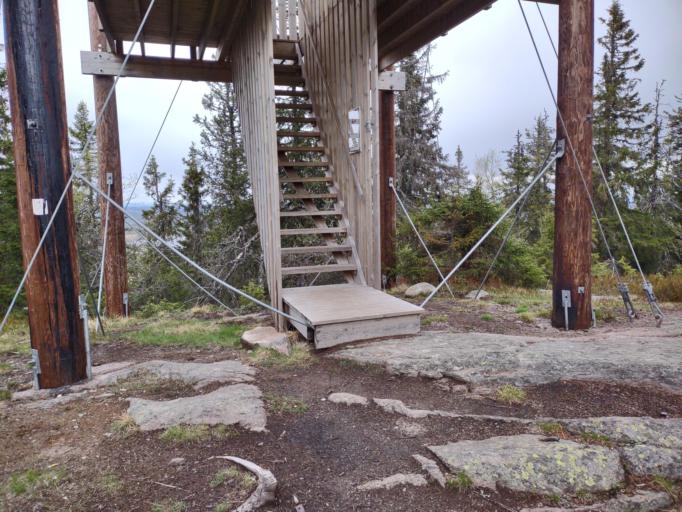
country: NO
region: Oppland
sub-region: Gran
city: Jaren
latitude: 60.4308
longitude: 10.6874
